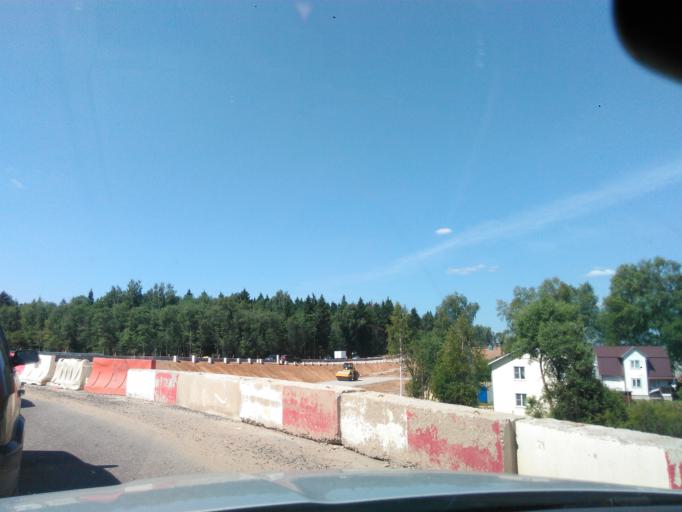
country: RU
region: Moskovskaya
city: Solnechnogorsk
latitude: 56.1555
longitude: 36.9215
